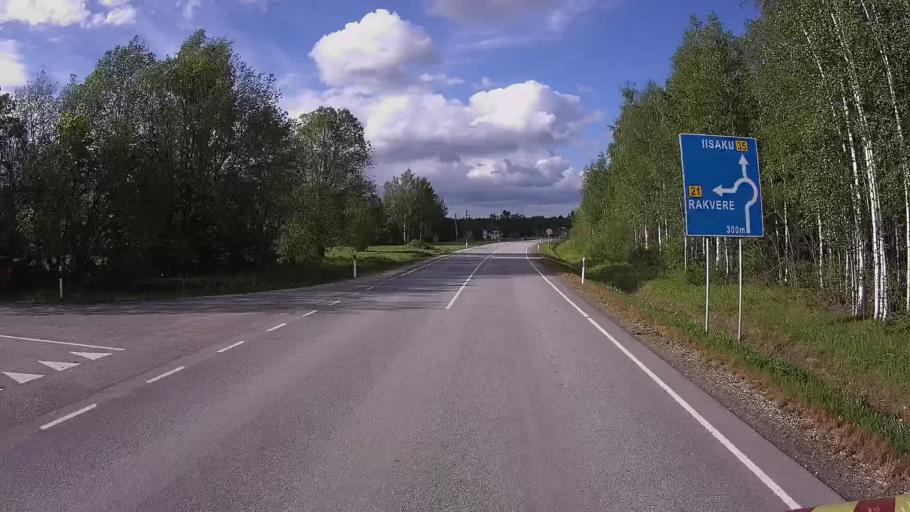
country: EE
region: Jogevamaa
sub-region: Mustvee linn
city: Mustvee
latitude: 58.9764
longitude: 26.8273
